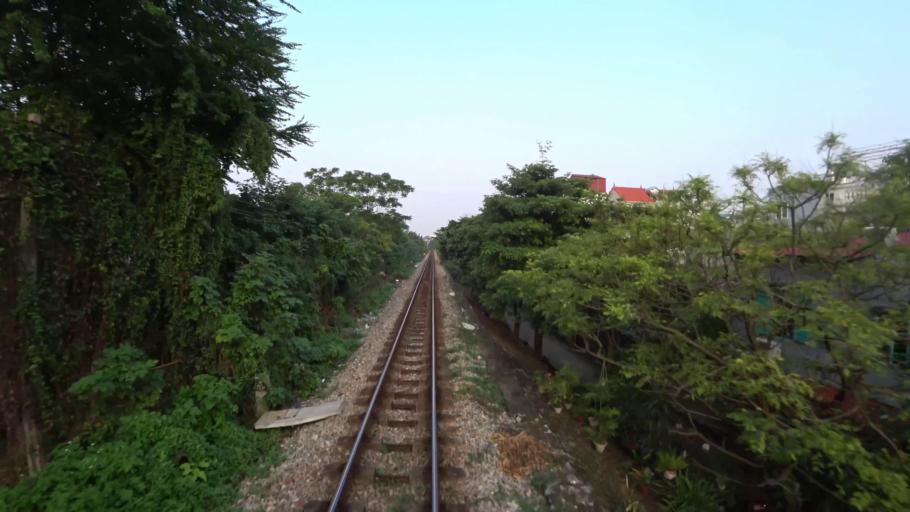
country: VN
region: Ha Noi
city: Hoan Kiem
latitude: 21.0503
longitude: 105.8759
